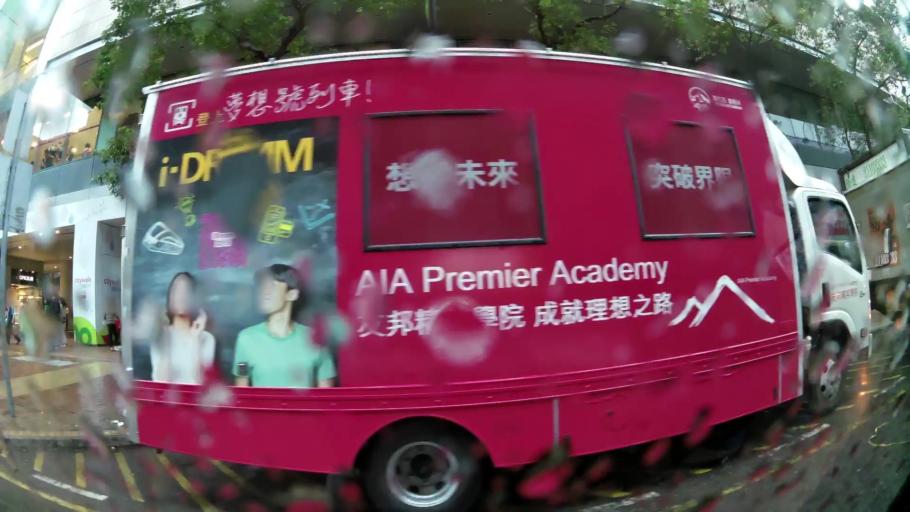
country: HK
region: Tsuen Wan
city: Tsuen Wan
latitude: 22.3698
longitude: 114.1147
